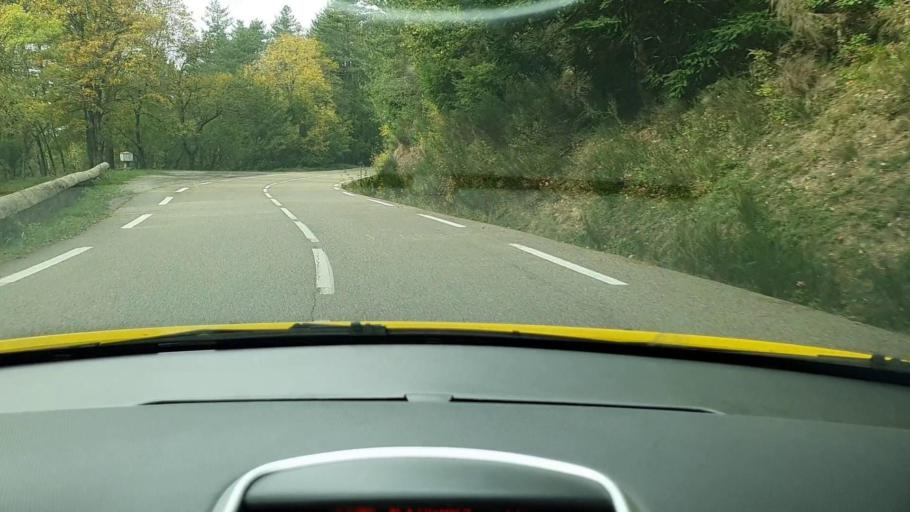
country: FR
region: Languedoc-Roussillon
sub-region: Departement de la Lozere
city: Meyrueis
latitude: 44.1267
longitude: 3.4451
